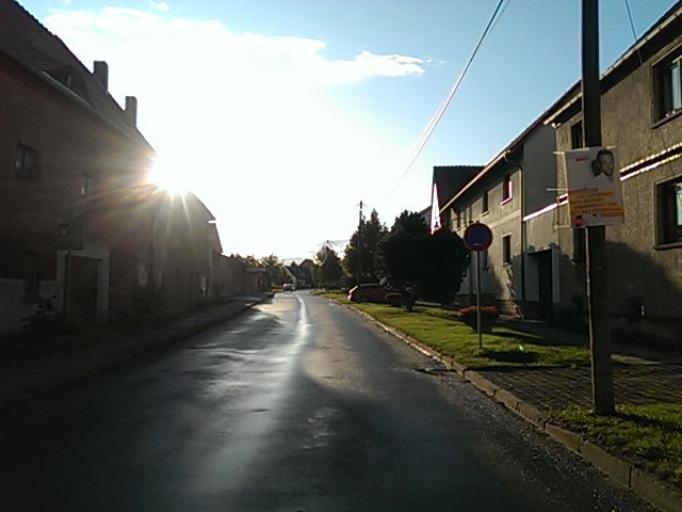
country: DE
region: Thuringia
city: Wiehe
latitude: 51.2222
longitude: 11.4107
